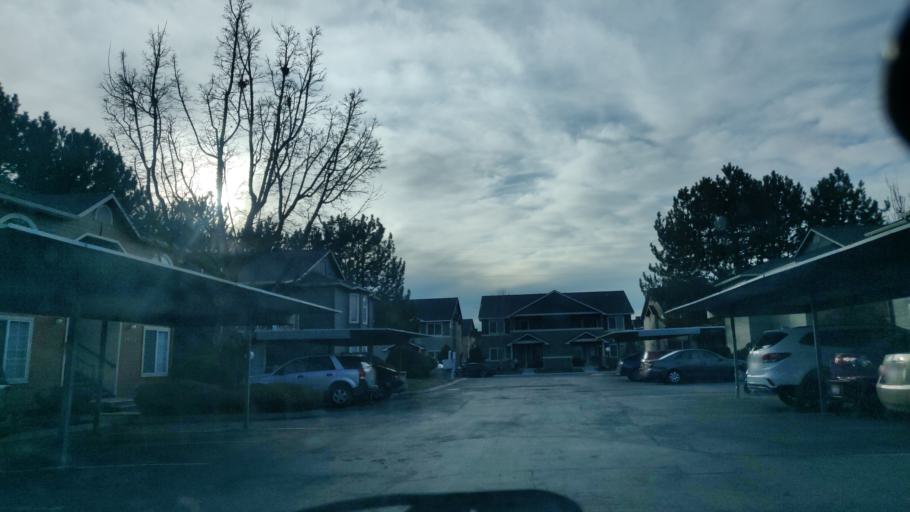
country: US
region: Idaho
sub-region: Ada County
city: Garden City
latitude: 43.6177
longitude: -116.2629
